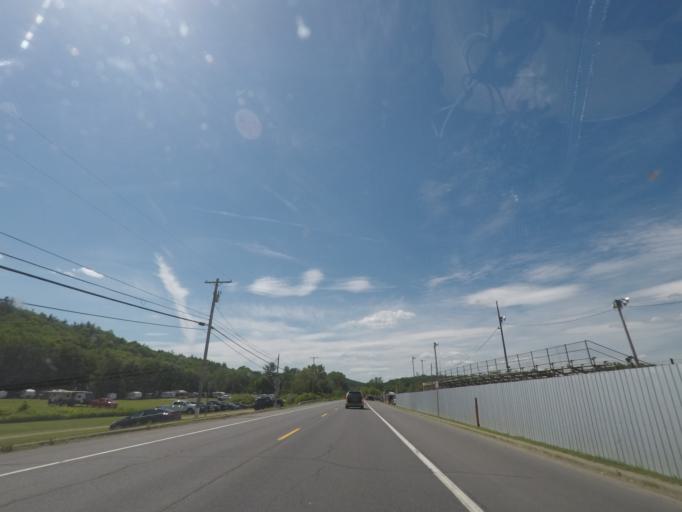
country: US
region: New York
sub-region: Rensselaer County
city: Nassau
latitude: 42.4911
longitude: -73.4895
